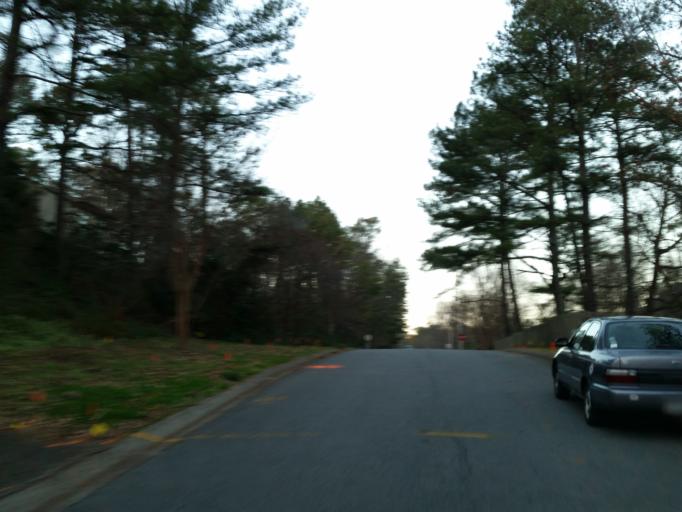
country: US
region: Georgia
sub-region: Fulton County
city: Sandy Springs
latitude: 33.9621
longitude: -84.4021
